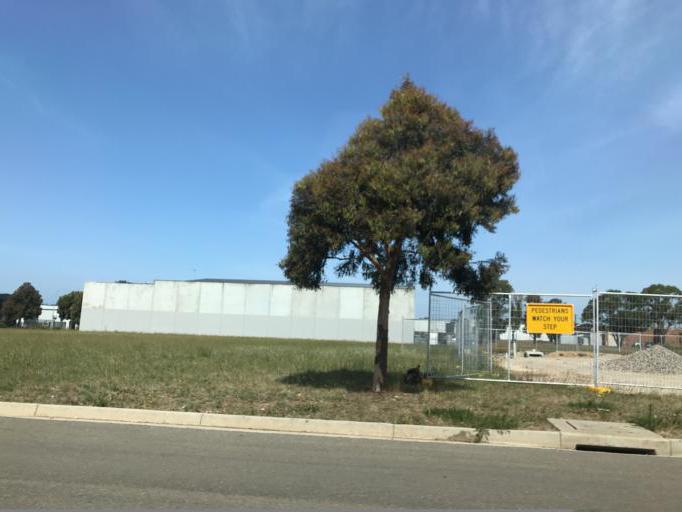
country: AU
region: Victoria
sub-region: Ballarat North
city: Newington
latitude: -37.5431
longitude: 143.7918
